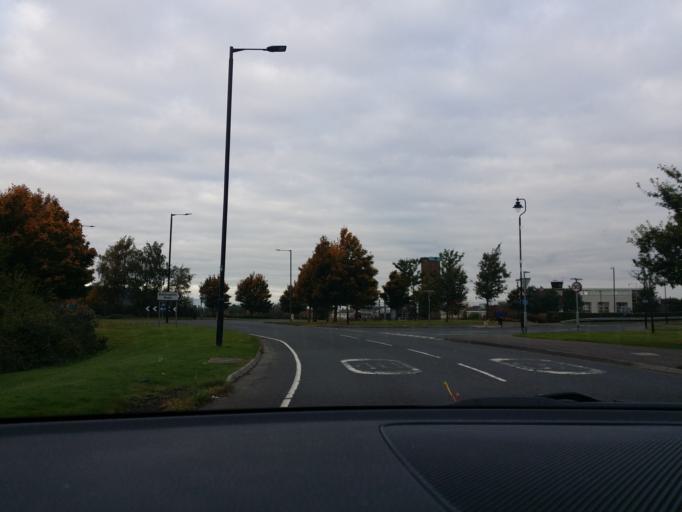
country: GB
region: Scotland
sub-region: Stirling
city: Stirling
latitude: 56.1244
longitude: -3.9533
